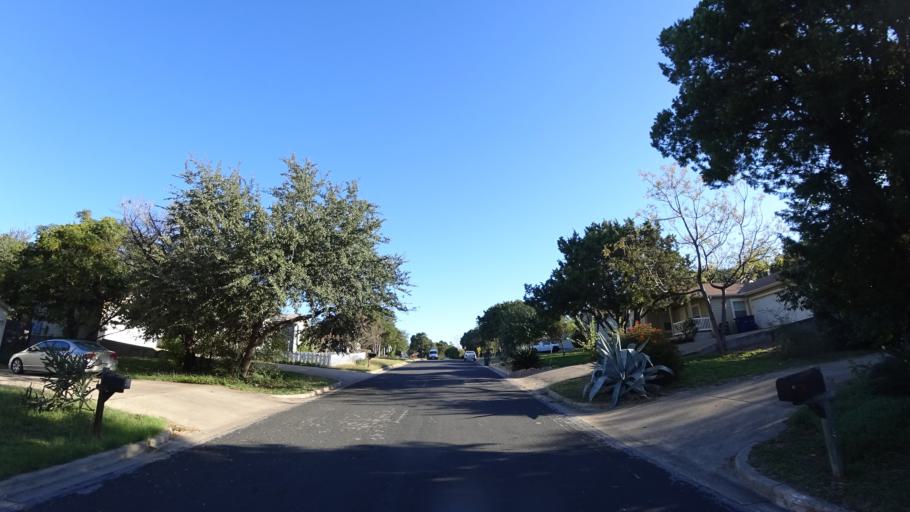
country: US
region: Texas
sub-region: Travis County
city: Austin
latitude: 30.2913
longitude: -97.6860
